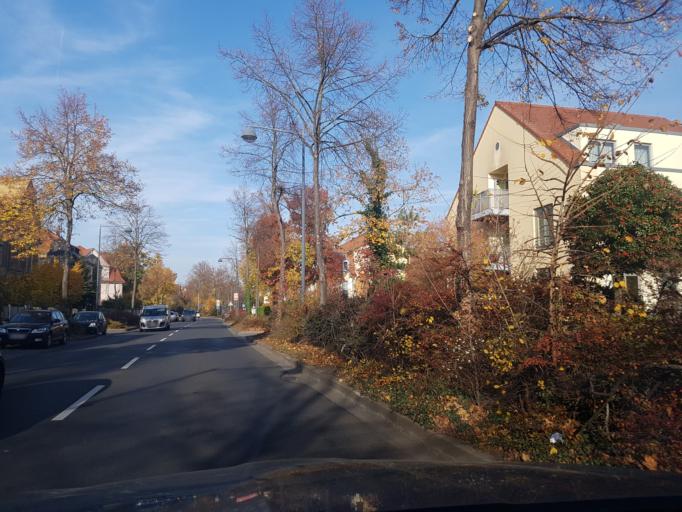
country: DE
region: Saxony
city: Torgau
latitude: 51.5561
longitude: 12.9977
